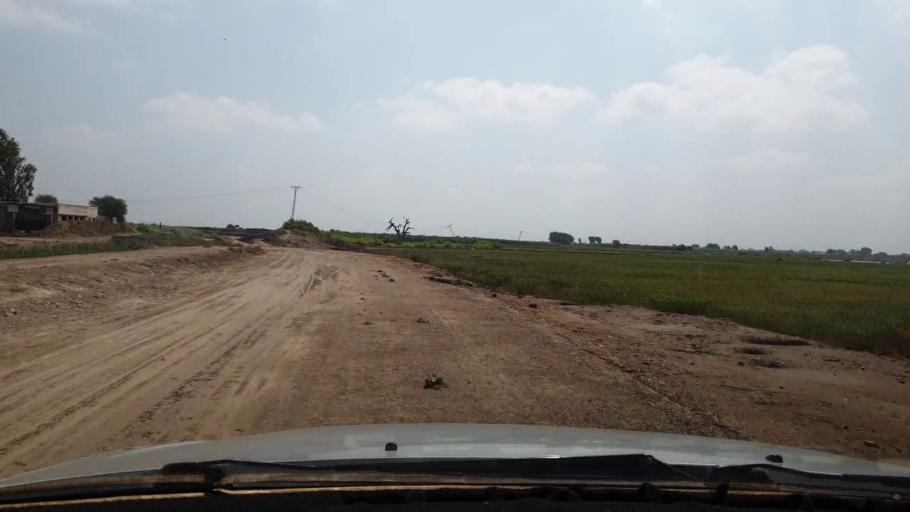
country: PK
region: Sindh
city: Matli
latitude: 25.0948
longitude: 68.6922
